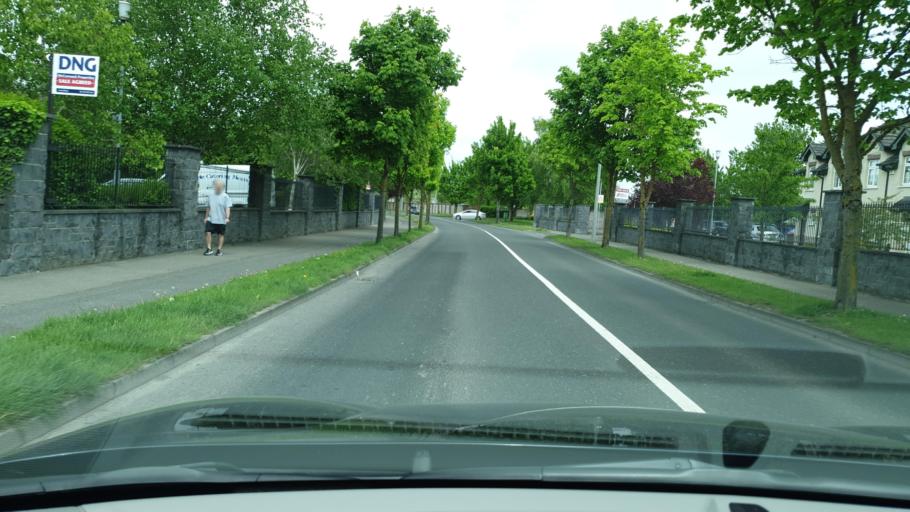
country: IE
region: Leinster
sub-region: Kildare
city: Clane
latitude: 53.2922
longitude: -6.6802
